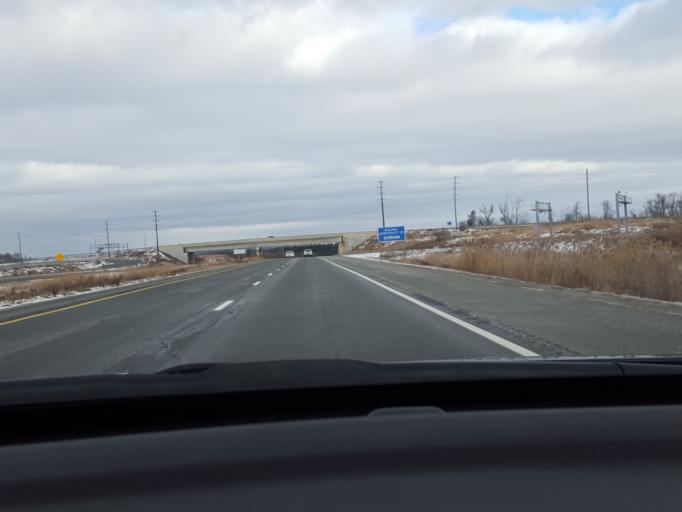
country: CA
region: Ontario
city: Pickering
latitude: 43.8881
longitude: -79.1882
